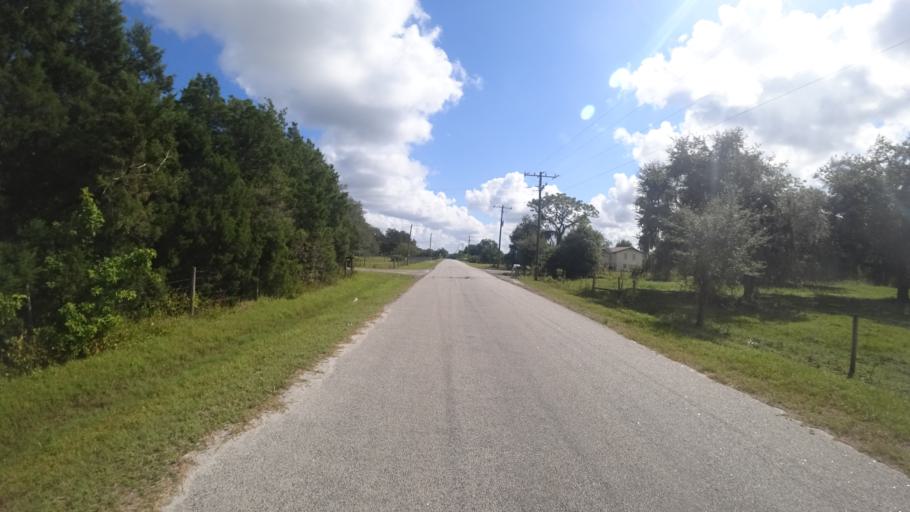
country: US
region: Florida
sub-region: Sarasota County
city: Lake Sarasota
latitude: 27.4012
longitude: -82.2644
